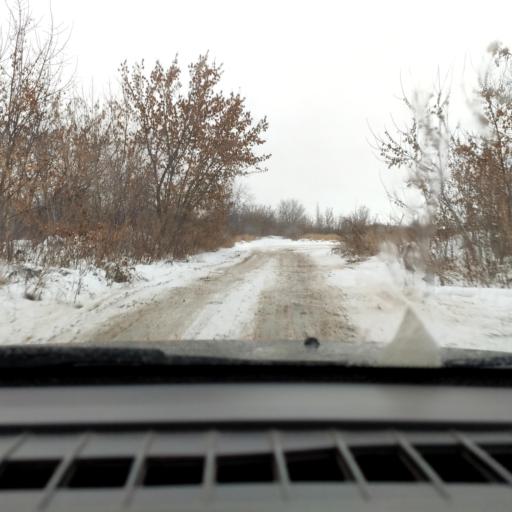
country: RU
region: Samara
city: Tol'yatti
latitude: 53.5628
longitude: 49.3267
